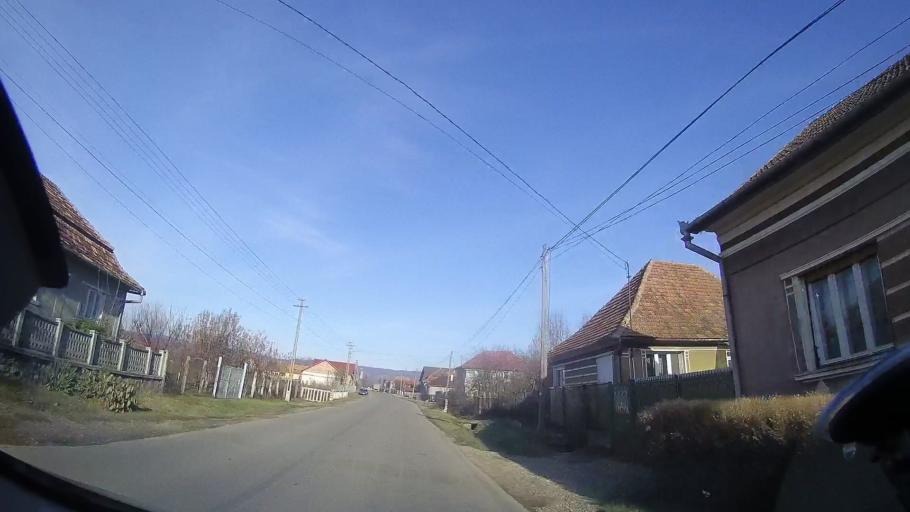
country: RO
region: Bihor
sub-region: Comuna Astileu
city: Astileu
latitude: 47.0314
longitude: 22.3886
